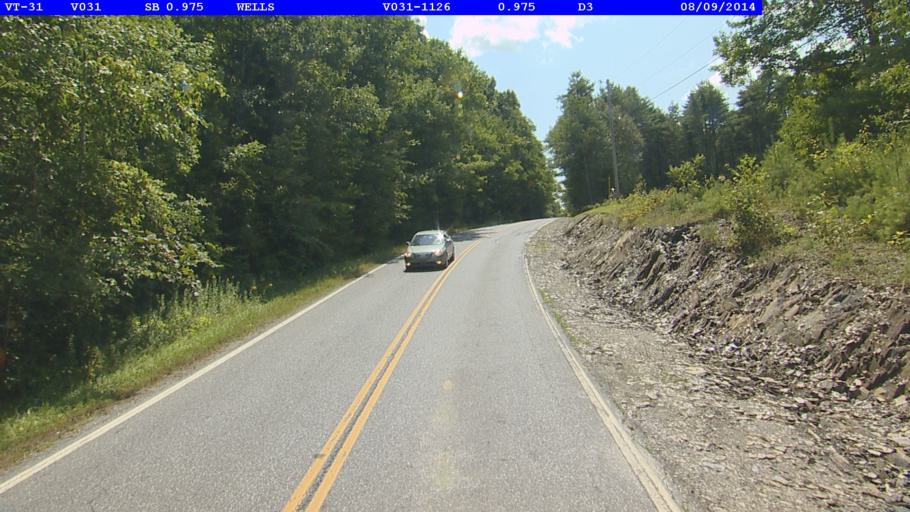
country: US
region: New York
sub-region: Washington County
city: Granville
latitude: 43.4513
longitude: -73.2433
